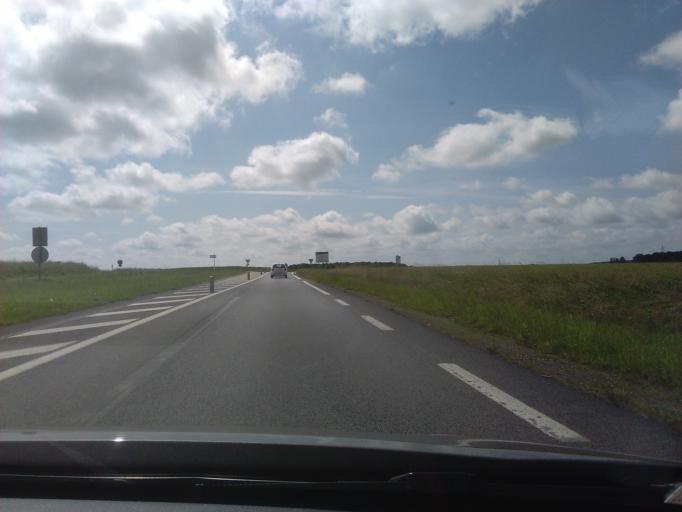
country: FR
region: Centre
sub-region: Departement du Loir-et-Cher
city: Vendome
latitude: 47.7704
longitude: 1.0883
